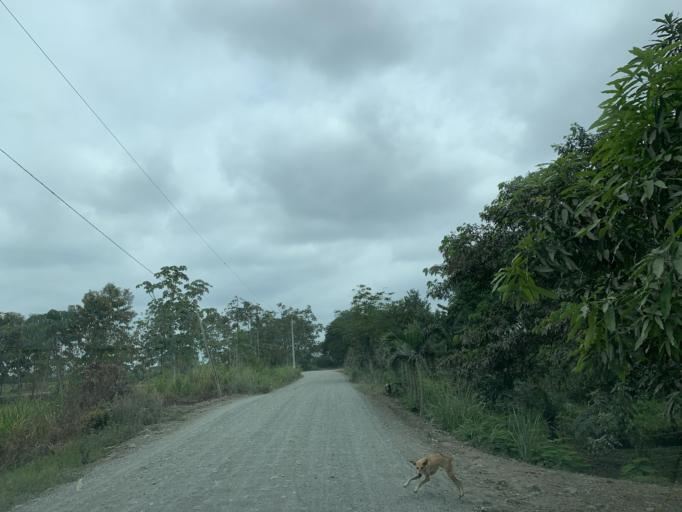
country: EC
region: Guayas
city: Coronel Marcelino Mariduena
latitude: -2.3204
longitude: -79.4704
